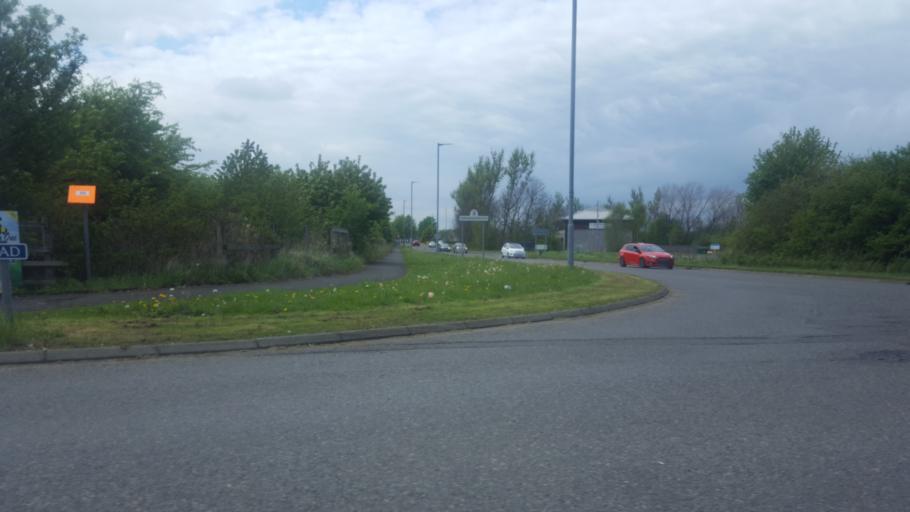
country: GB
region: Scotland
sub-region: Falkirk
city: Polmont
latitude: 56.0007
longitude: -3.7054
